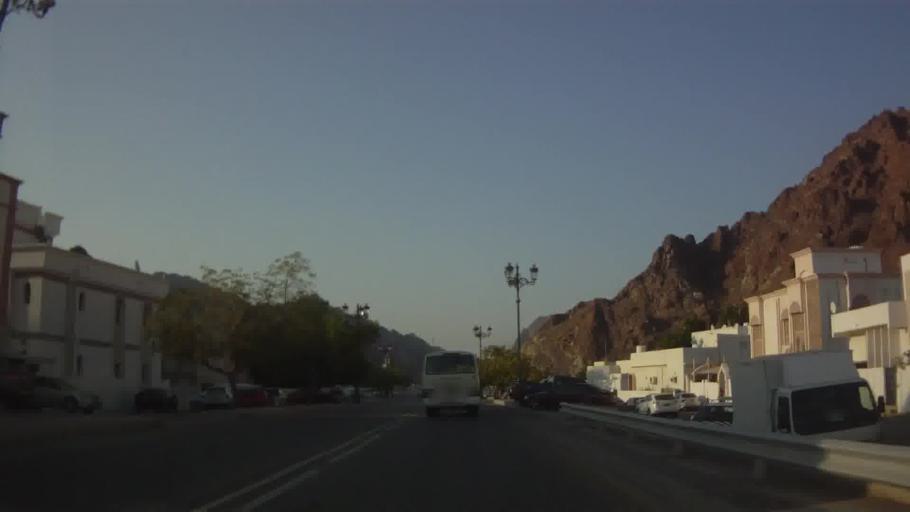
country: OM
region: Muhafazat Masqat
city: Muscat
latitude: 23.5926
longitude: 58.5984
